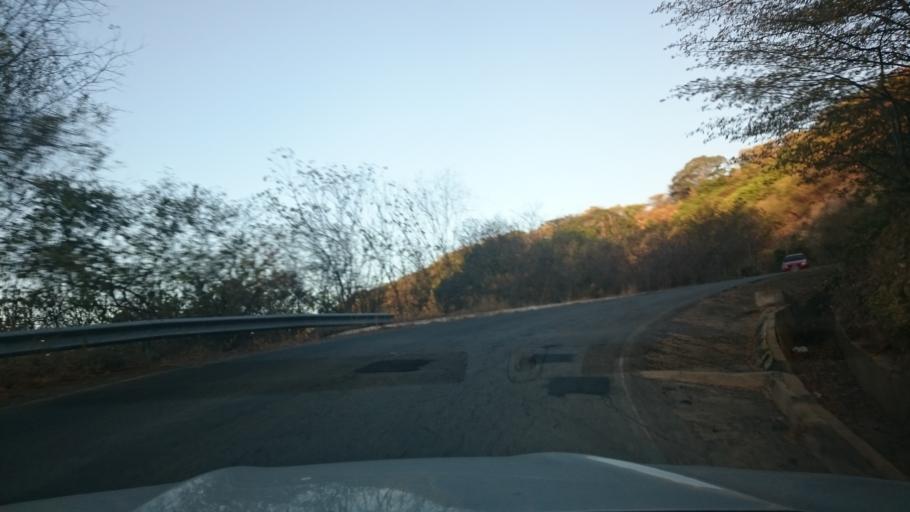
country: BR
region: Rio Grande do Norte
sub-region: Umarizal
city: Umarizal
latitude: -6.0188
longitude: -37.9910
